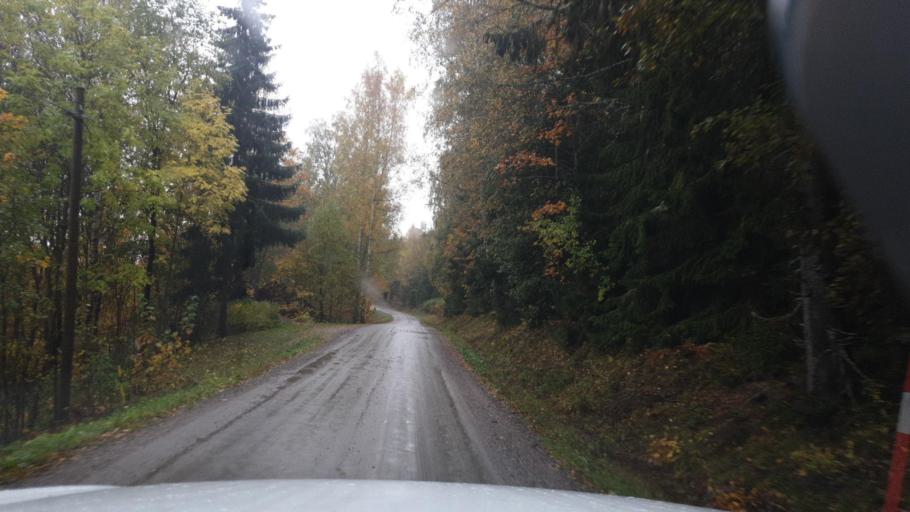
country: SE
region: Vaermland
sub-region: Eda Kommun
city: Amotfors
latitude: 59.7396
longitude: 12.2777
